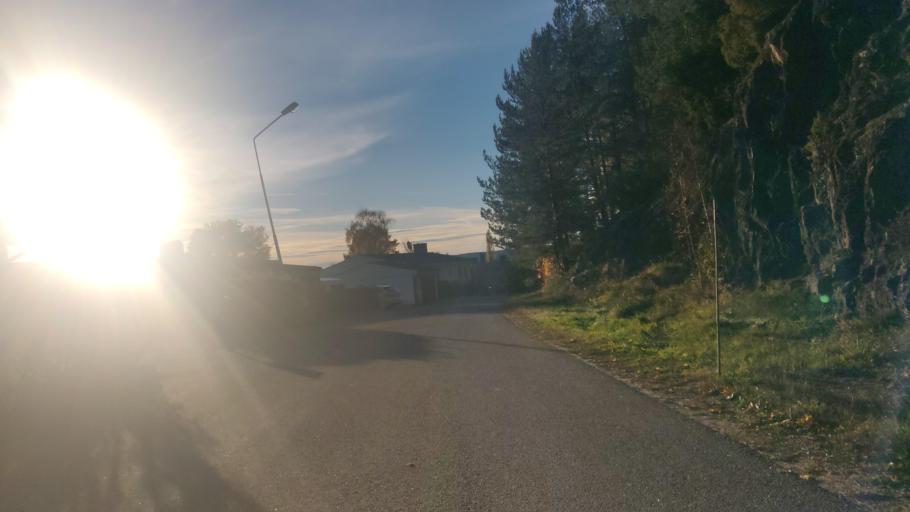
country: SE
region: Vaesternorrland
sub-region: Sundsvalls Kommun
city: Njurundabommen
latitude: 62.2728
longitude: 17.4023
